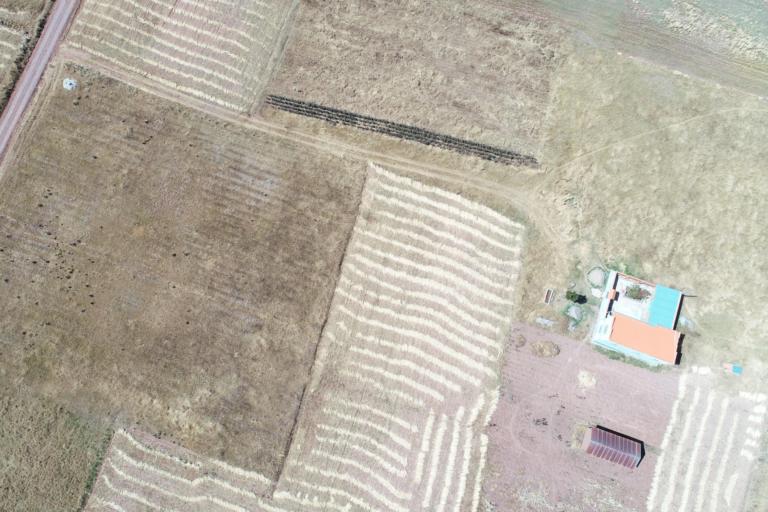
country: BO
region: La Paz
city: Tiahuanaco
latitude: -16.5949
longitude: -68.7749
